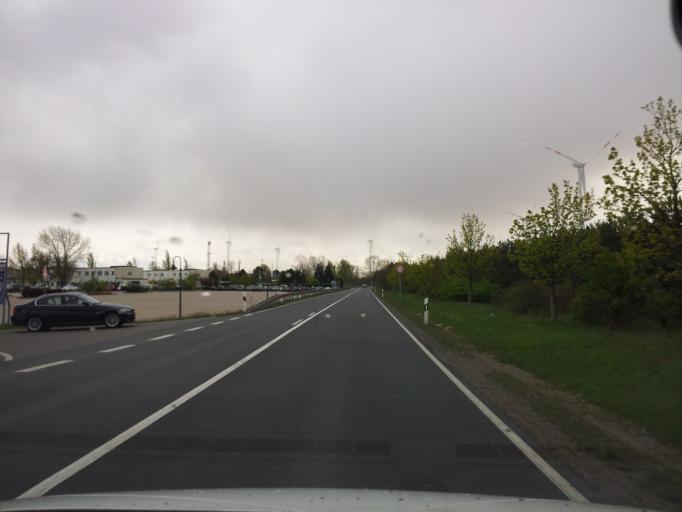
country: DE
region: Brandenburg
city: Heinersbruck
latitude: 51.7915
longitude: 14.4841
